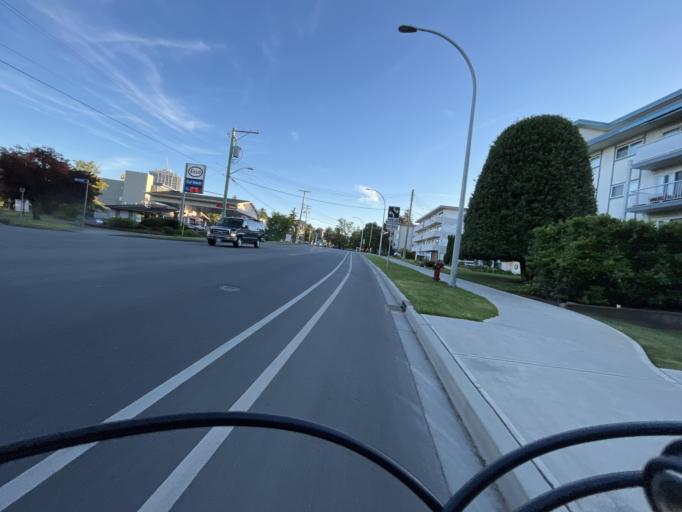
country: CA
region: British Columbia
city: Victoria
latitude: 48.4280
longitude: -123.3343
